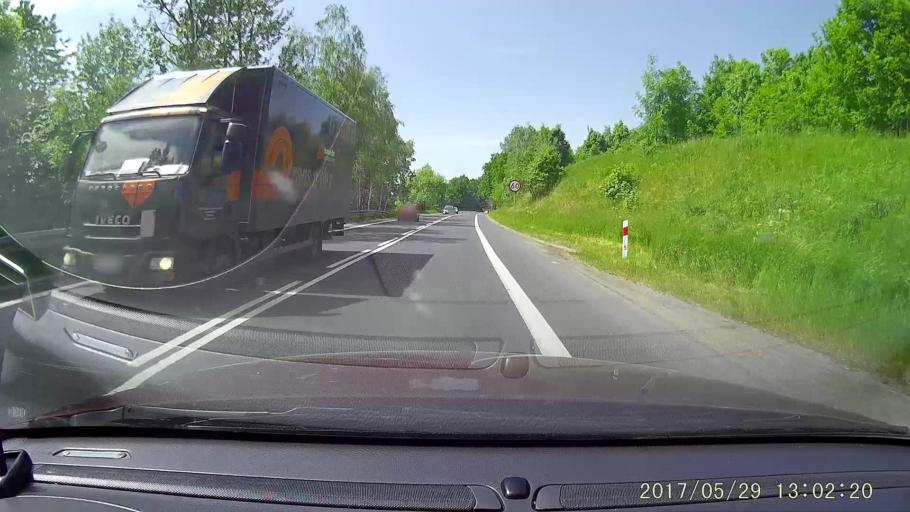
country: PL
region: Lower Silesian Voivodeship
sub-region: Powiat jeleniogorski
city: Stara Kamienica
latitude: 50.9137
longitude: 15.6292
